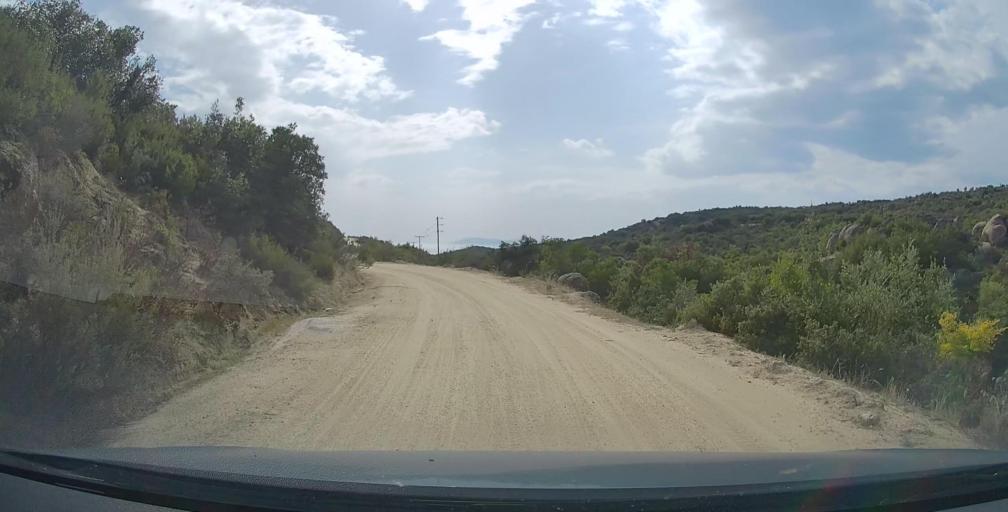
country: GR
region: Central Macedonia
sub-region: Nomos Chalkidikis
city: Sykia
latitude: 40.0003
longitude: 23.9272
